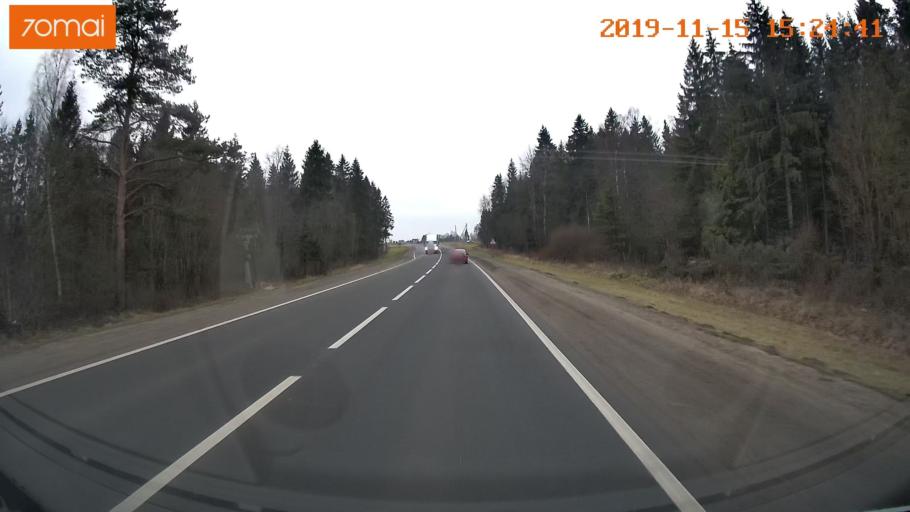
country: RU
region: Jaroslavl
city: Danilov
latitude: 58.1742
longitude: 40.1333
